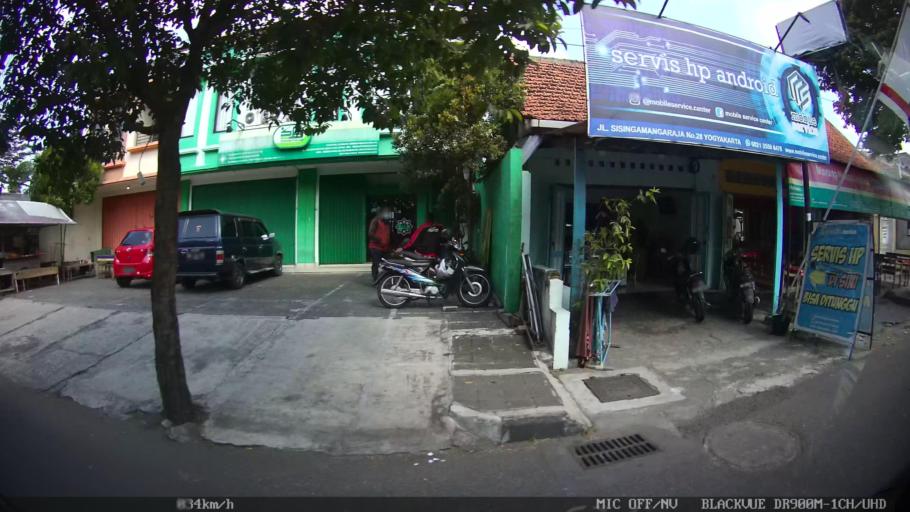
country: ID
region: Daerah Istimewa Yogyakarta
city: Yogyakarta
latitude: -7.8168
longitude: 110.3731
